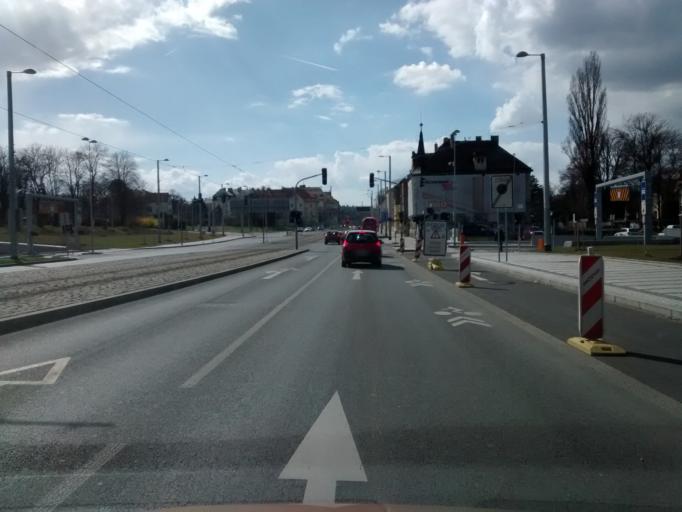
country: CZ
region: Praha
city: Prague
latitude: 50.0985
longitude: 14.4126
